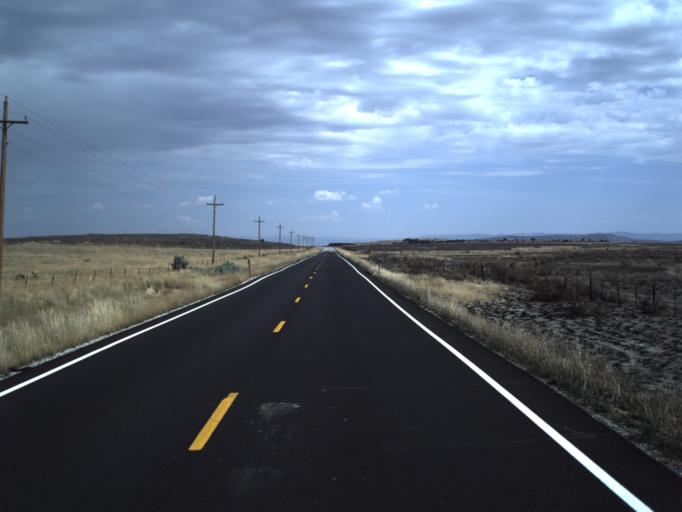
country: US
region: Idaho
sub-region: Minidoka County
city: Rupert
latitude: 41.8251
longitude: -113.1786
